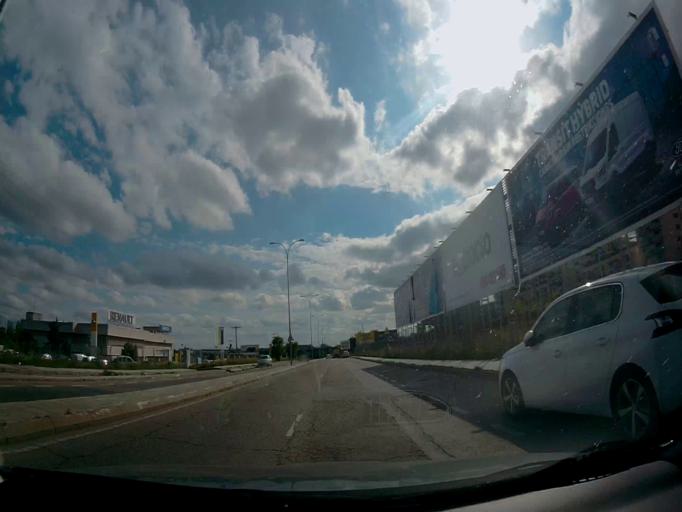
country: ES
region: Madrid
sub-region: Provincia de Madrid
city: Alcorcon
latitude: 40.3404
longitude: -3.8437
